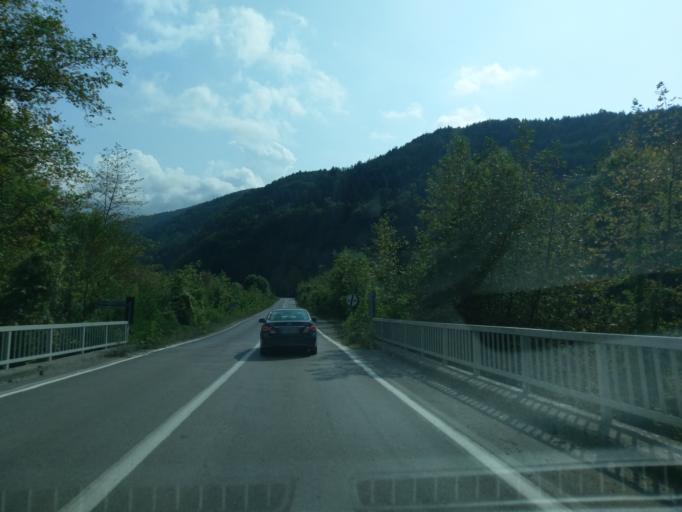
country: TR
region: Sinop
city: Yenikonak
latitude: 41.8776
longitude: 34.5501
